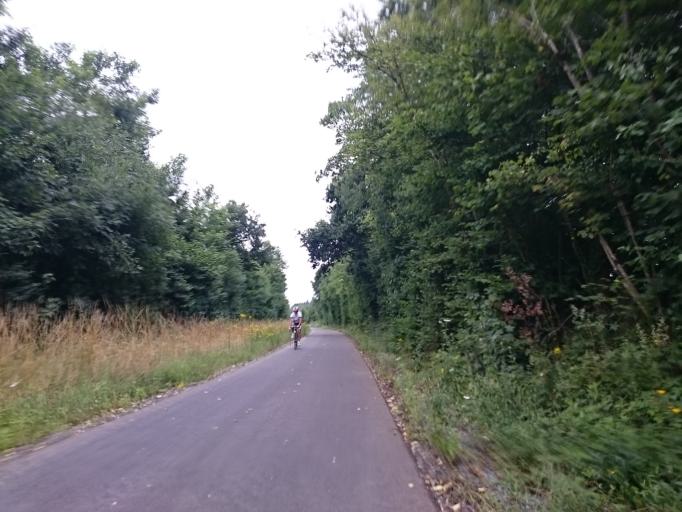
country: FR
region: Lower Normandy
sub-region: Departement du Calvados
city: Bully
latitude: 49.0894
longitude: -0.4219
